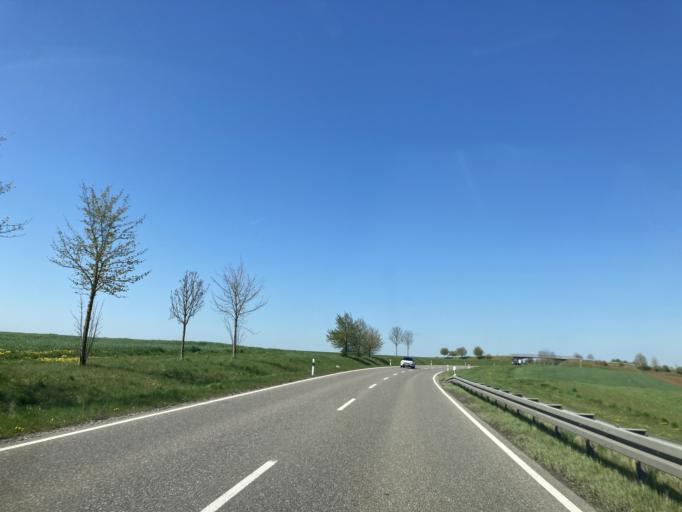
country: DE
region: Baden-Wuerttemberg
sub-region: Regierungsbezirk Stuttgart
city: Motzingen
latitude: 48.5077
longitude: 8.7948
